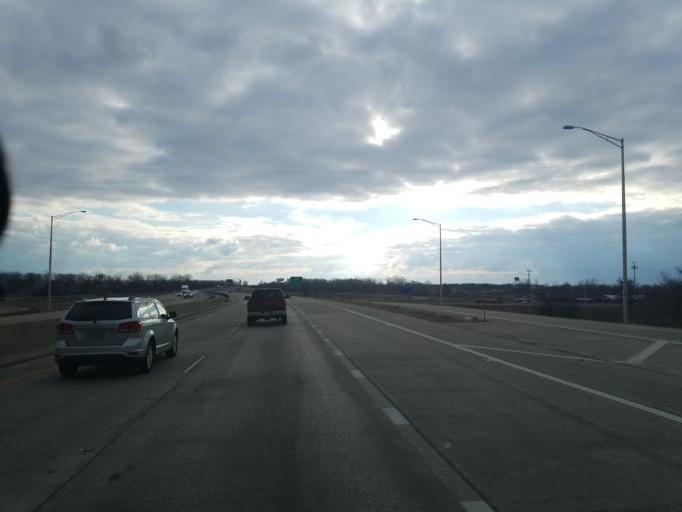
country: US
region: Illinois
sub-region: Madison County
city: Mitchell
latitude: 38.7660
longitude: -90.1280
